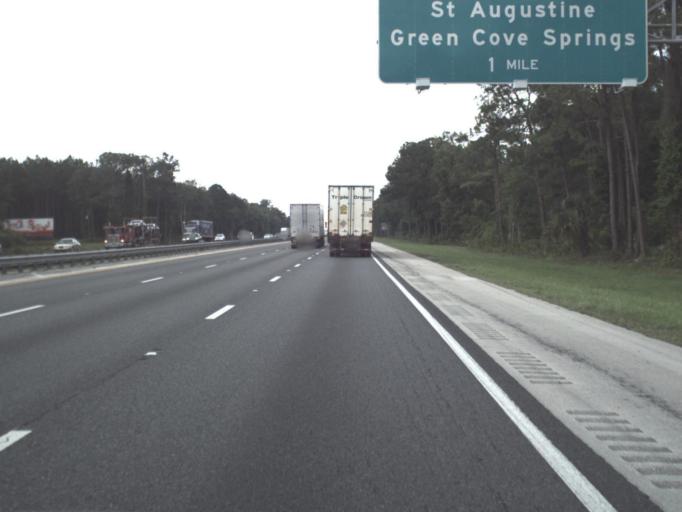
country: US
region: Florida
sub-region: Saint Johns County
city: Saint Augustine
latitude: 29.8989
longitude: -81.4062
